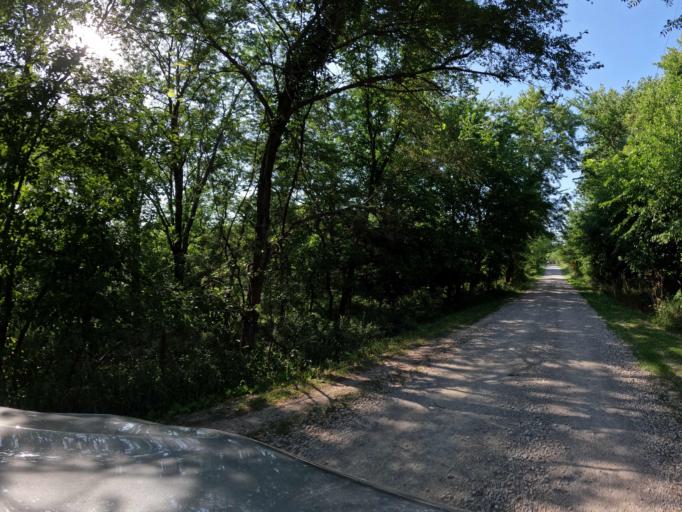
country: US
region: Iowa
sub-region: Appanoose County
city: Centerville
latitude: 40.7300
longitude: -93.0159
